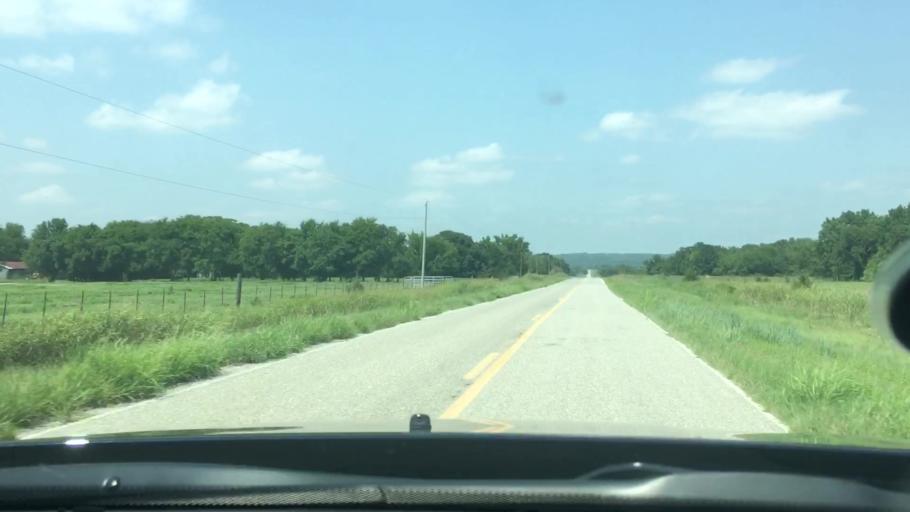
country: US
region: Oklahoma
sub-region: Johnston County
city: Tishomingo
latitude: 34.3836
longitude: -96.4962
